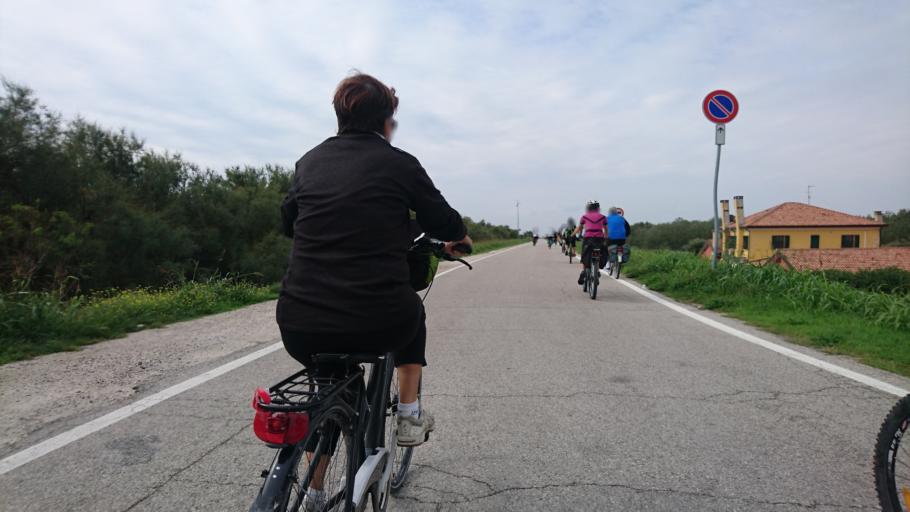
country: IT
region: Veneto
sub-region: Provincia di Rovigo
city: Scardovari
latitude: 44.8440
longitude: 12.4642
